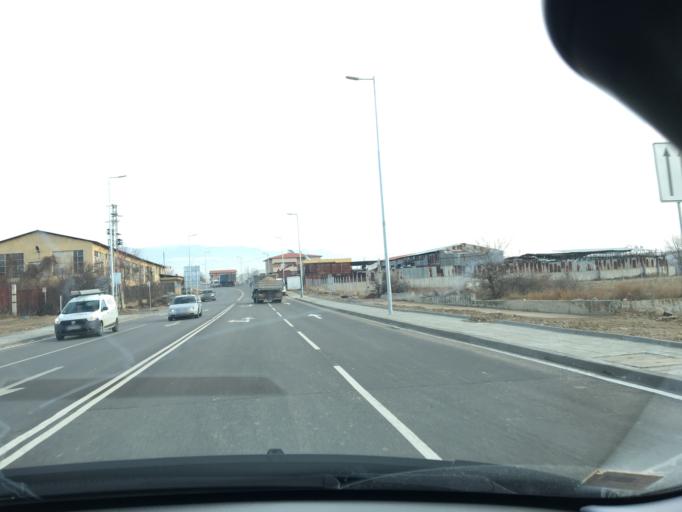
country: BG
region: Blagoevgrad
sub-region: Obshtina Sandanski
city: Sandanski
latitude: 41.5417
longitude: 23.2573
